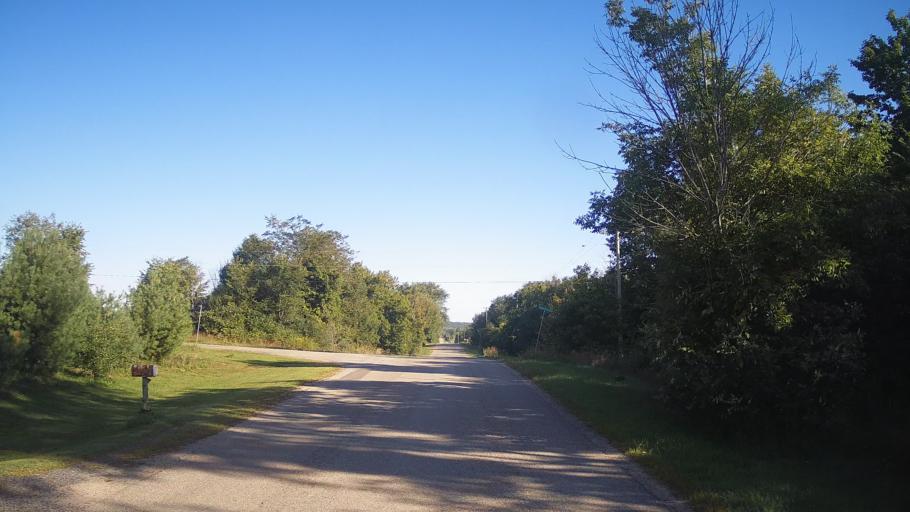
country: US
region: New York
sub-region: Jefferson County
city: Alexandria Bay
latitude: 44.4493
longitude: -75.9849
